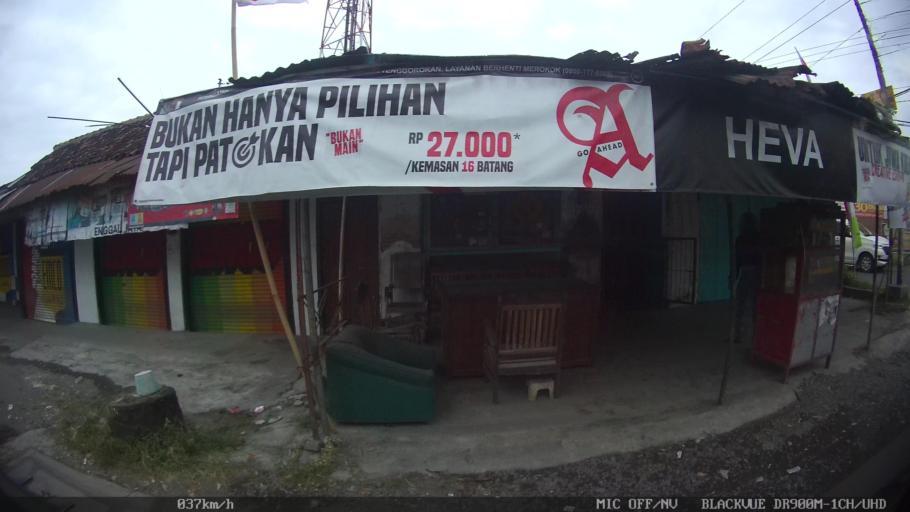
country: ID
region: Daerah Istimewa Yogyakarta
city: Sewon
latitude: -7.8435
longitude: 110.3911
